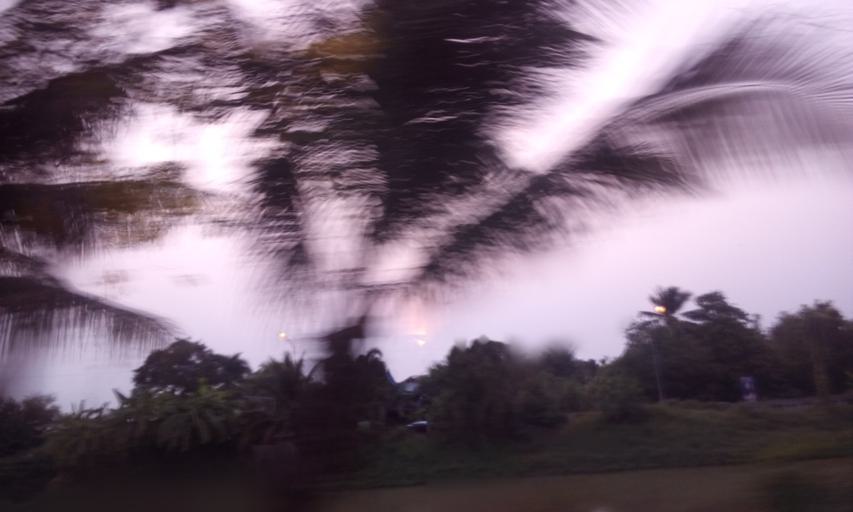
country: TH
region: Pathum Thani
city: Nong Suea
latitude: 14.0301
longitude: 100.8939
